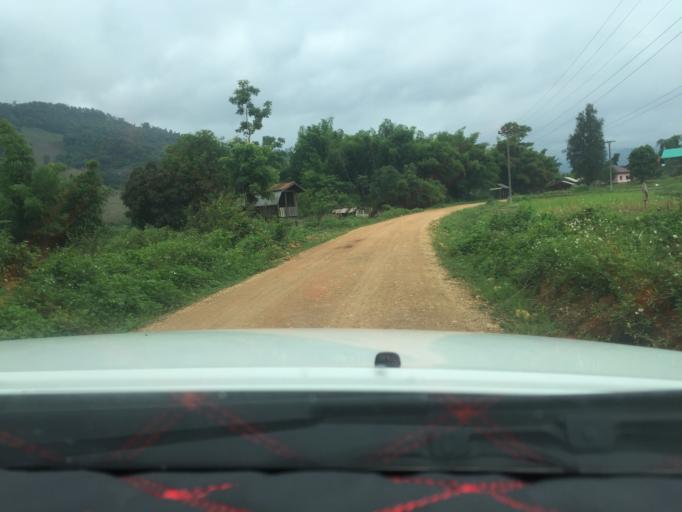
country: TH
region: Phayao
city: Phu Sang
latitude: 19.6822
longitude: 100.5024
